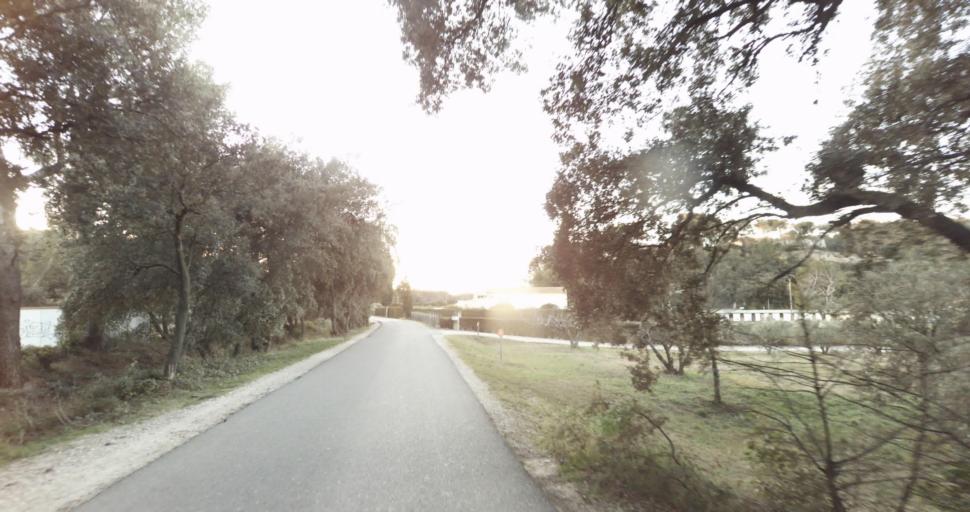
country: FR
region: Provence-Alpes-Cote d'Azur
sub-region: Departement des Bouches-du-Rhone
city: Barbentane
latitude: 43.8838
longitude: 4.7665
